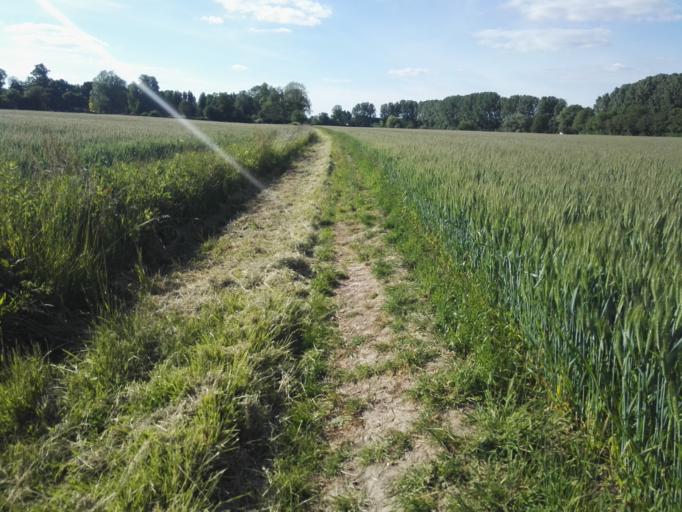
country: FR
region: Haute-Normandie
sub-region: Departement de l'Eure
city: Pacy-sur-Eure
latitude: 48.9933
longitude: 1.3941
